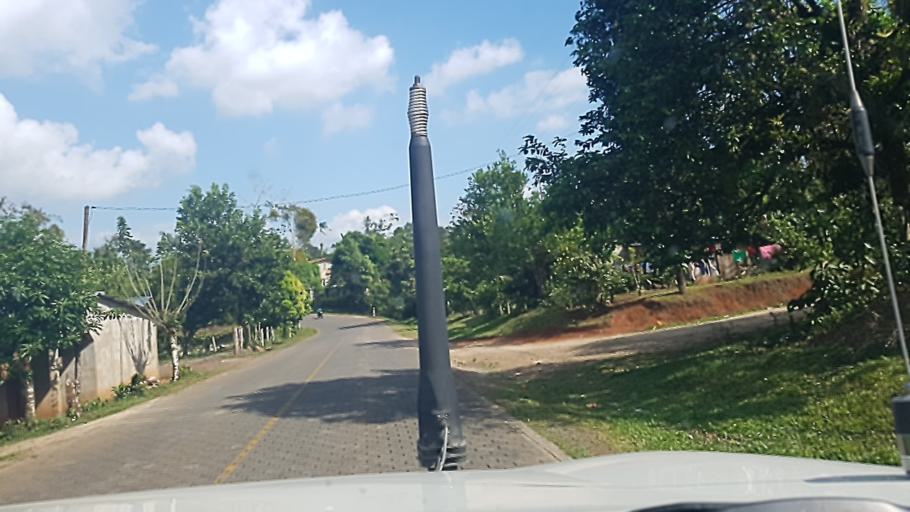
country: NI
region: Atlantico Sur
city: Nueva Guinea
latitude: 11.7031
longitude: -84.3739
